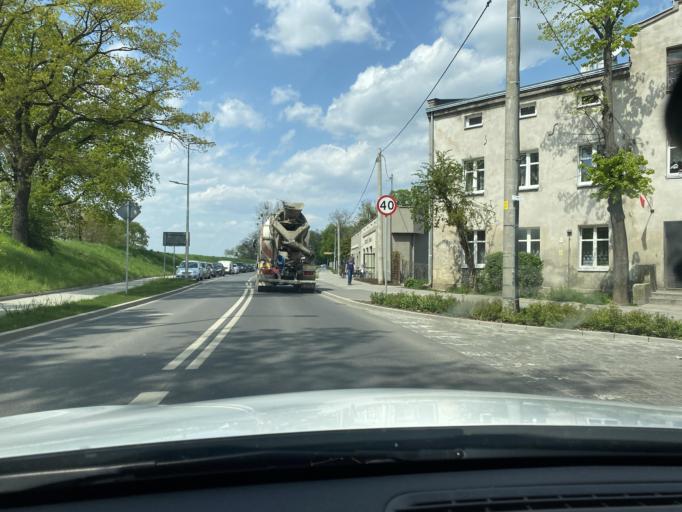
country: PL
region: Lower Silesian Voivodeship
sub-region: Powiat wroclawski
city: Wroclaw
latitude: 51.1378
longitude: 16.9933
